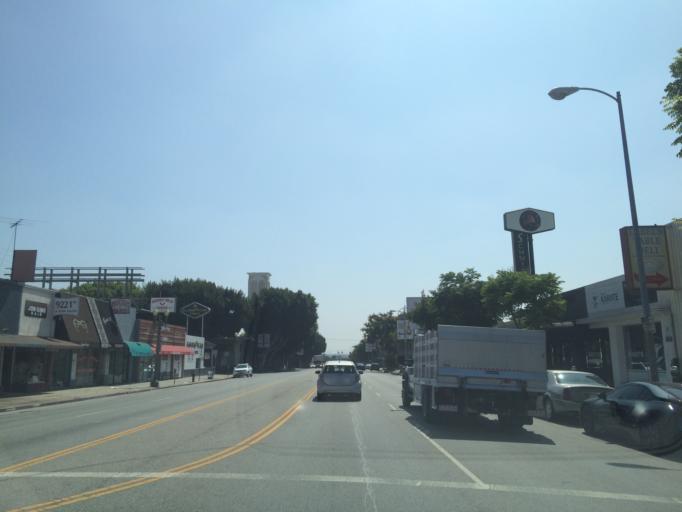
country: US
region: California
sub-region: Los Angeles County
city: Beverly Hills
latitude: 34.0553
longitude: -118.3928
